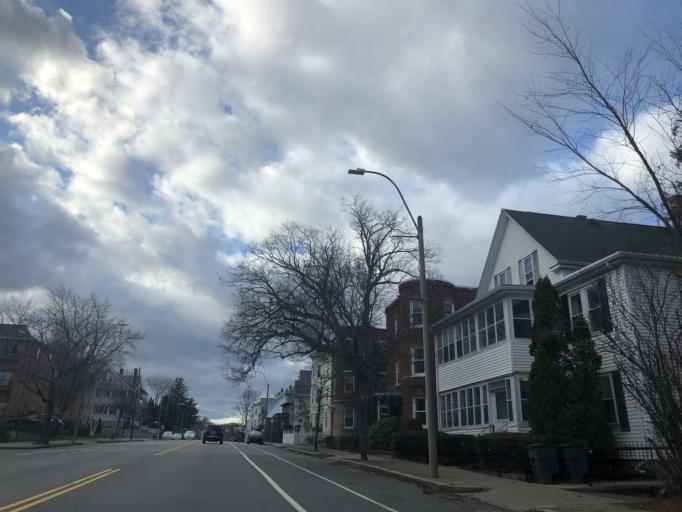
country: US
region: Massachusetts
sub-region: Middlesex County
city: Arlington
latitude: 42.4242
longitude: -71.1785
